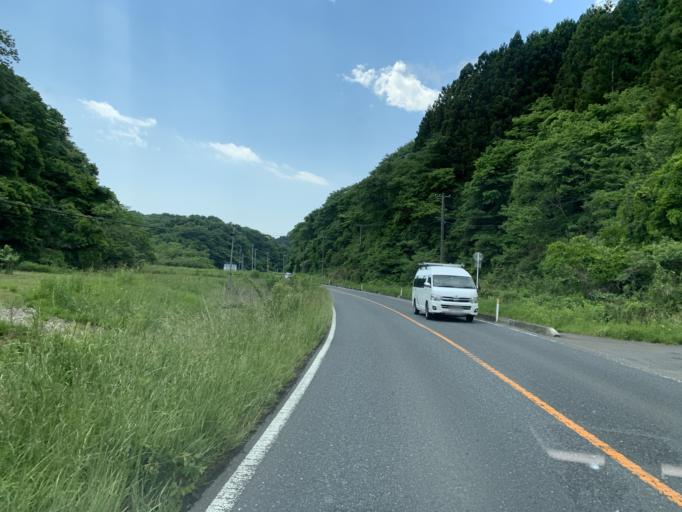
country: JP
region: Miyagi
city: Matsushima
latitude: 38.4134
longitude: 141.0634
